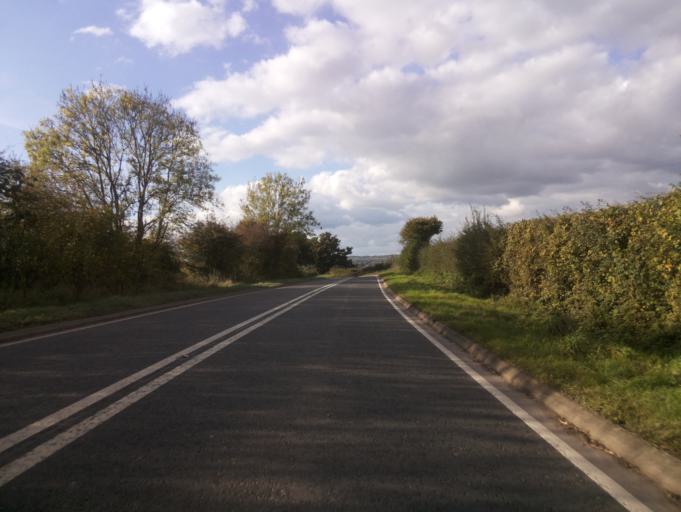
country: GB
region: England
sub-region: Herefordshire
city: Kinnersley
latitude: 52.1192
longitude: -2.9890
